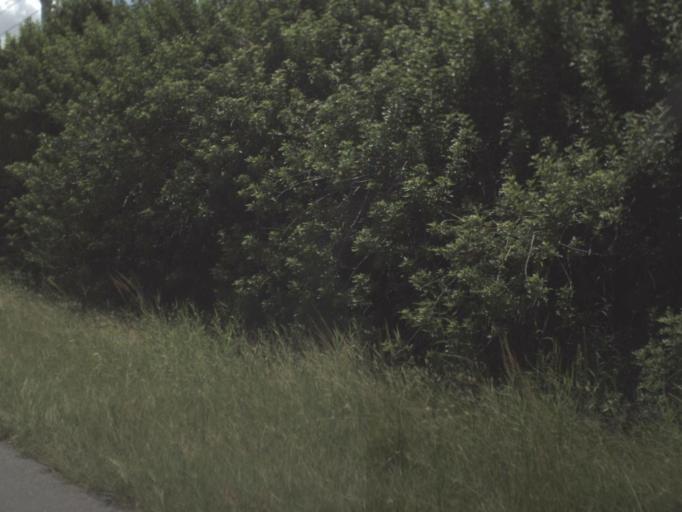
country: US
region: Florida
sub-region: Hillsborough County
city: Apollo Beach
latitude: 27.7926
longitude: -82.3896
